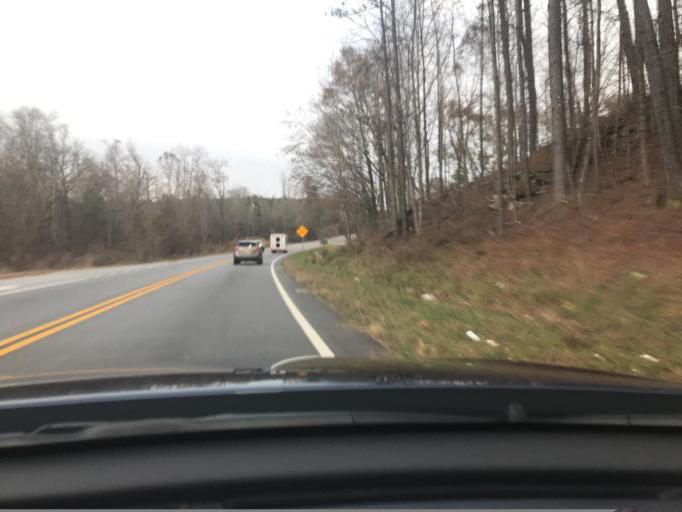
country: US
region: Georgia
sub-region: Newton County
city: Porterdale
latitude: 33.5821
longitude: -83.9217
